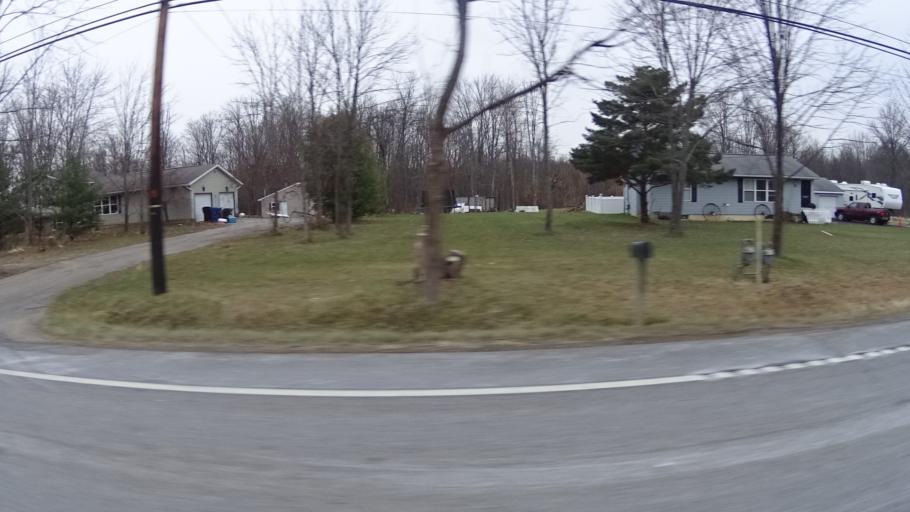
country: US
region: Ohio
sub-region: Lorain County
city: Grafton
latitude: 41.2603
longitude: -82.0283
